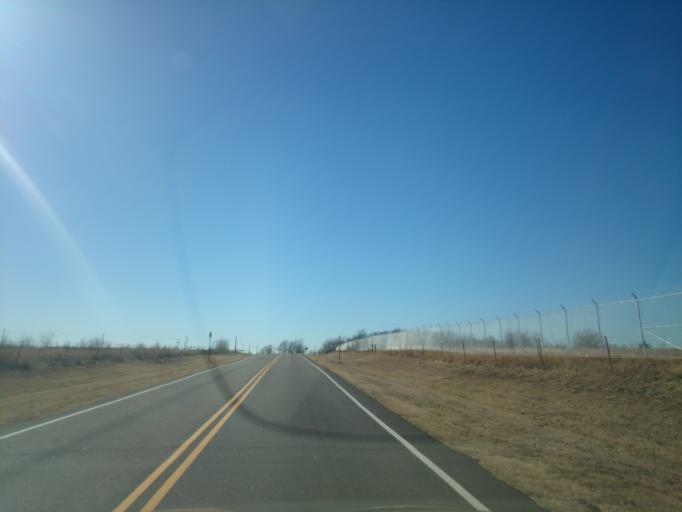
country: US
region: Oklahoma
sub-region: Payne County
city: Stillwater
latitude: 36.1477
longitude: -97.0860
